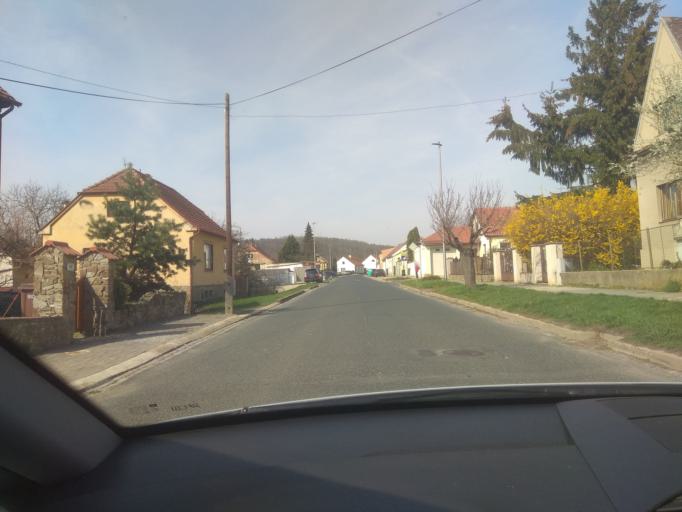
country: CZ
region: South Moravian
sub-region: Okres Brno-Venkov
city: Rosice
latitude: 49.1792
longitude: 16.3955
